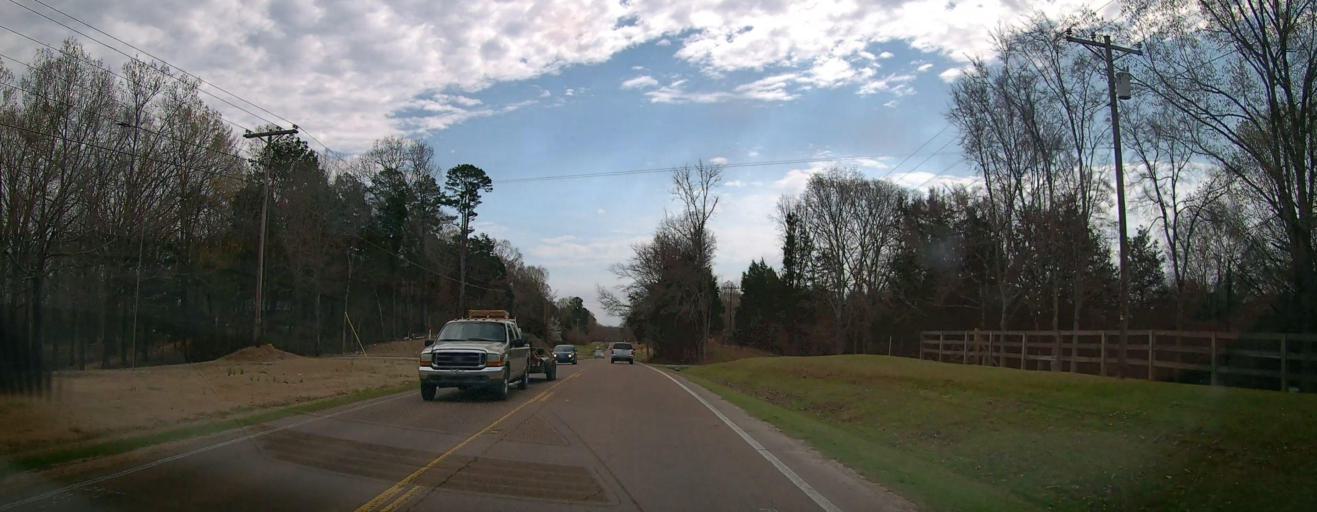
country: US
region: Mississippi
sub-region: De Soto County
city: Olive Branch
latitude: 34.9241
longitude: -89.7812
